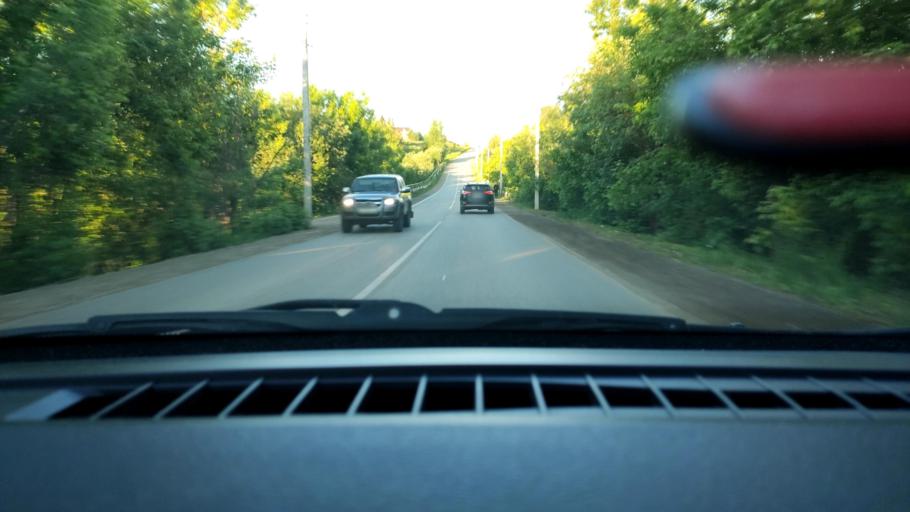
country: RU
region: Perm
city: Kultayevo
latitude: 57.9252
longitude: 55.8964
